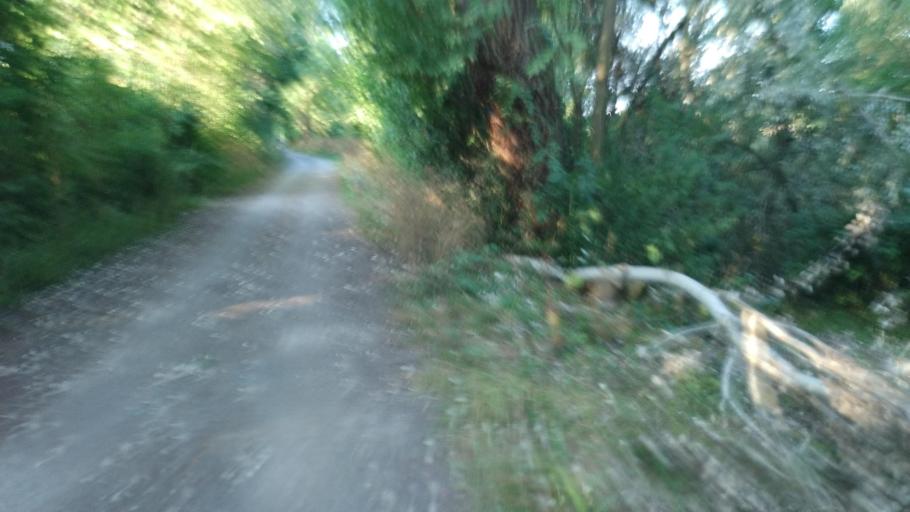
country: DE
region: Baden-Wuerttemberg
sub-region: Karlsruhe Region
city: Weingarten
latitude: 49.0324
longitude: 8.4700
